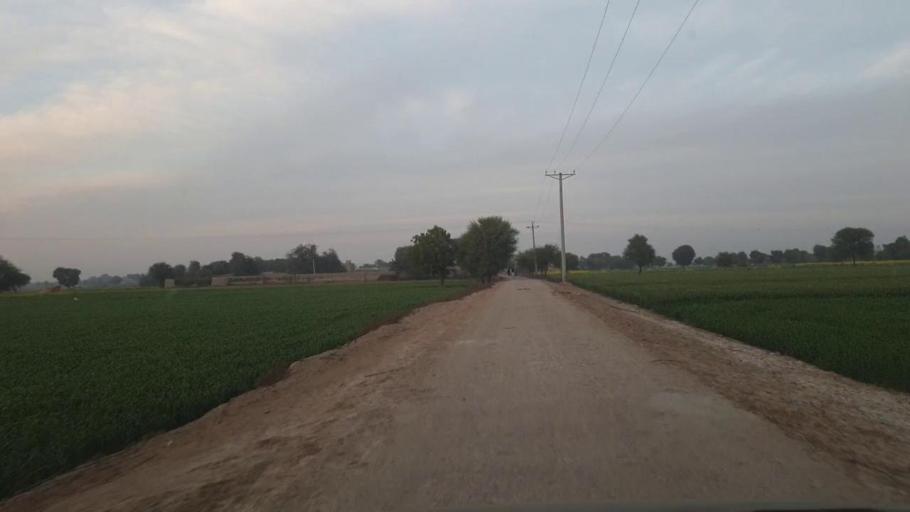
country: PK
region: Sindh
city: Shahpur Chakar
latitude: 26.0666
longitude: 68.5363
